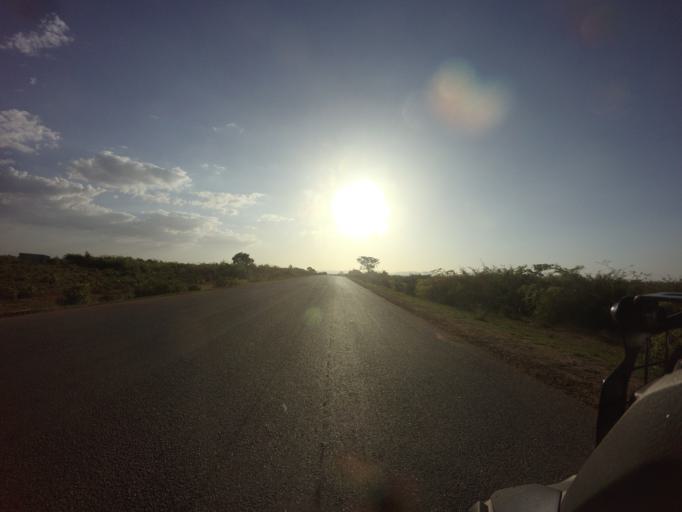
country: AO
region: Huila
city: Lubango
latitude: -14.8025
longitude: 13.6722
